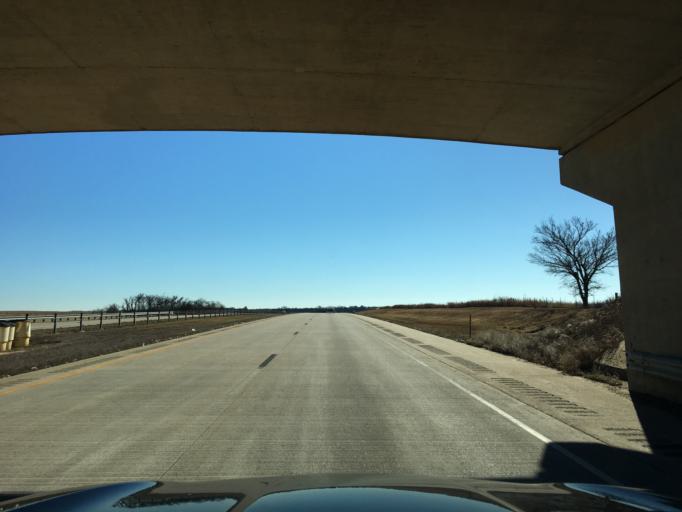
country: US
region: Oklahoma
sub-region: Kay County
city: Tonkawa
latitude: 36.4928
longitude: -97.3308
